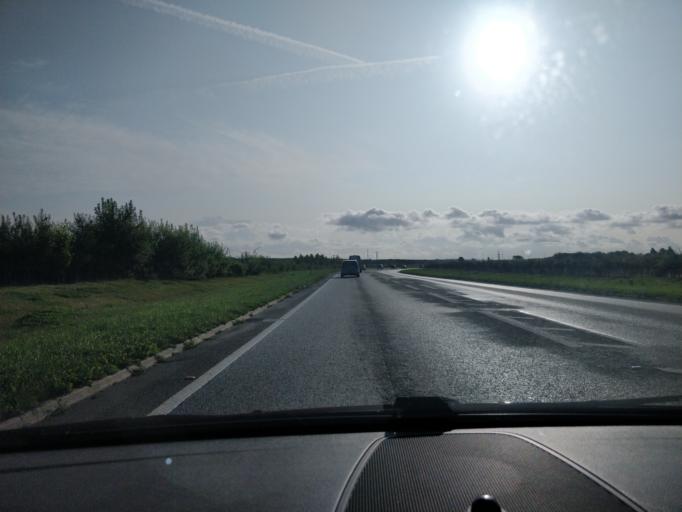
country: GB
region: England
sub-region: Sefton
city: Thornton
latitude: 53.4973
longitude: -2.9728
